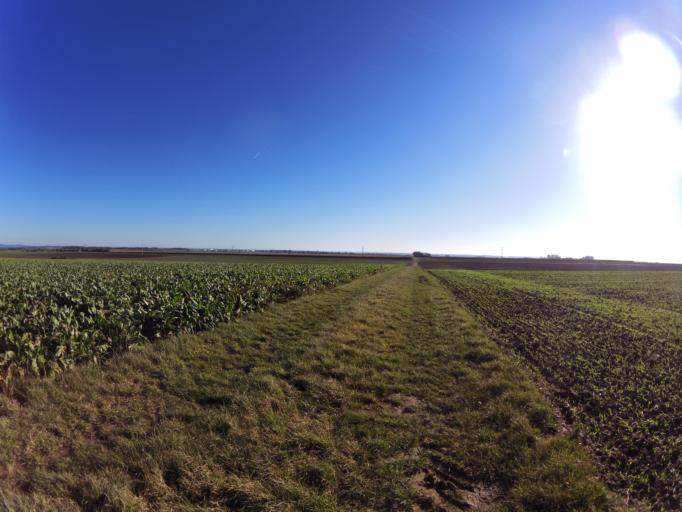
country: DE
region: Bavaria
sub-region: Regierungsbezirk Unterfranken
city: Giebelstadt
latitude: 49.6776
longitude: 9.9335
